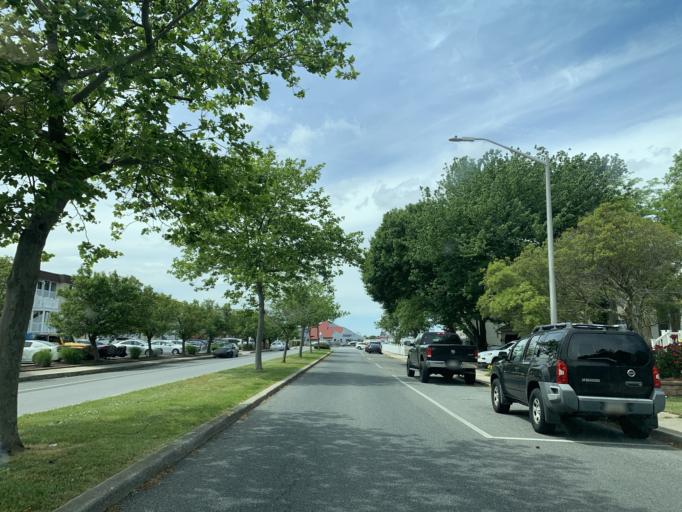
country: US
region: Delaware
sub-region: Sussex County
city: Bethany Beach
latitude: 38.4503
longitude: -75.0612
